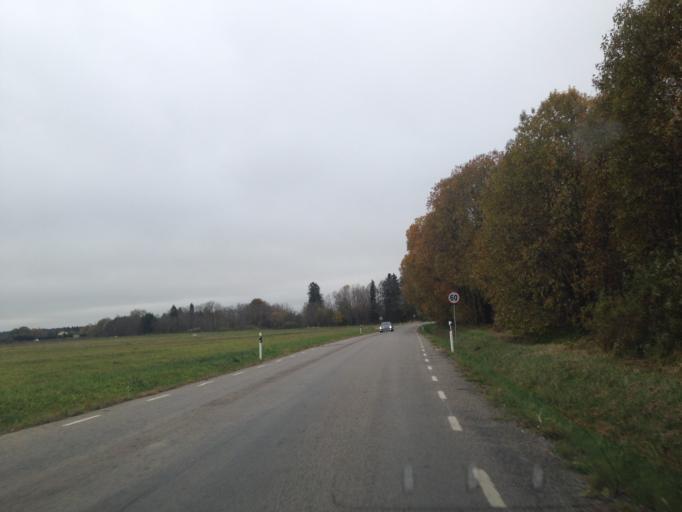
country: EE
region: Harju
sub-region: Saue linn
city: Saue
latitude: 59.3607
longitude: 24.5527
